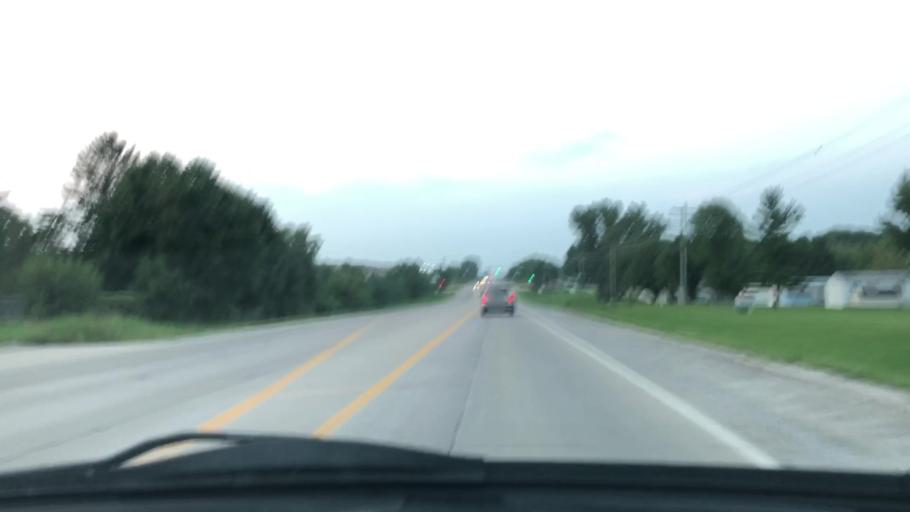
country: US
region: Iowa
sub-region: Johnson County
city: North Liberty
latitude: 41.7350
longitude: -91.6076
